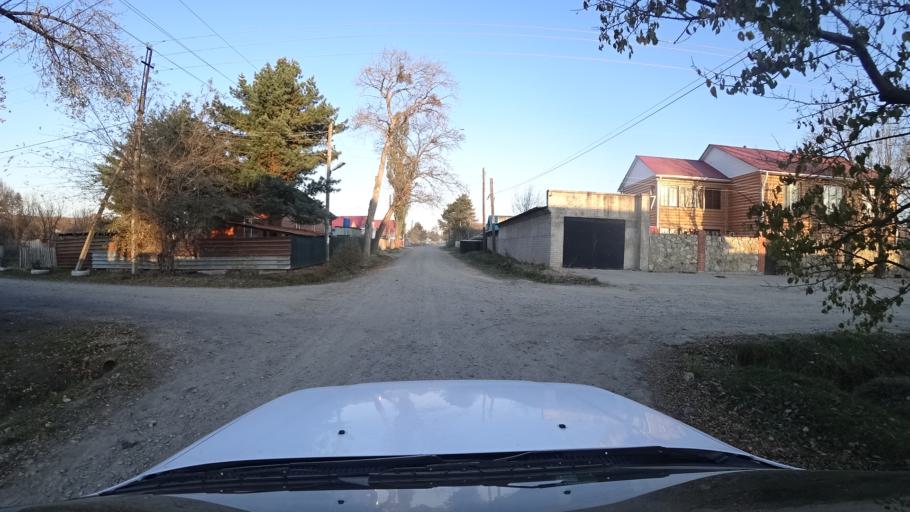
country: RU
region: Primorskiy
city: Dal'nerechensk
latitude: 45.9258
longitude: 133.7199
